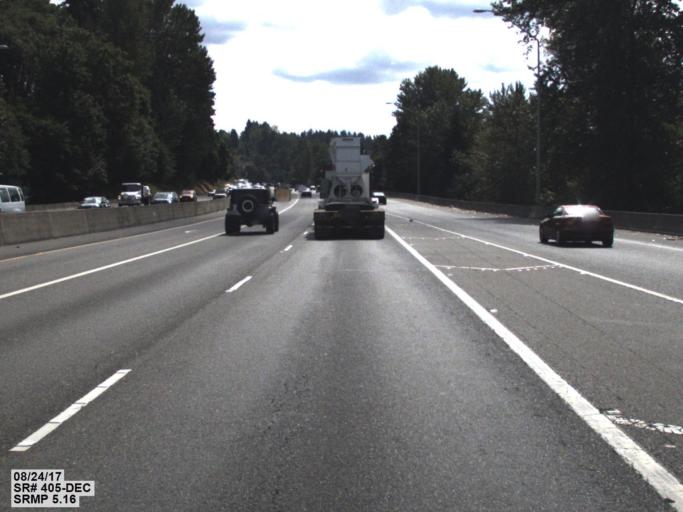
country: US
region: Washington
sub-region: King County
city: Renton
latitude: 47.4990
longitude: -122.1954
